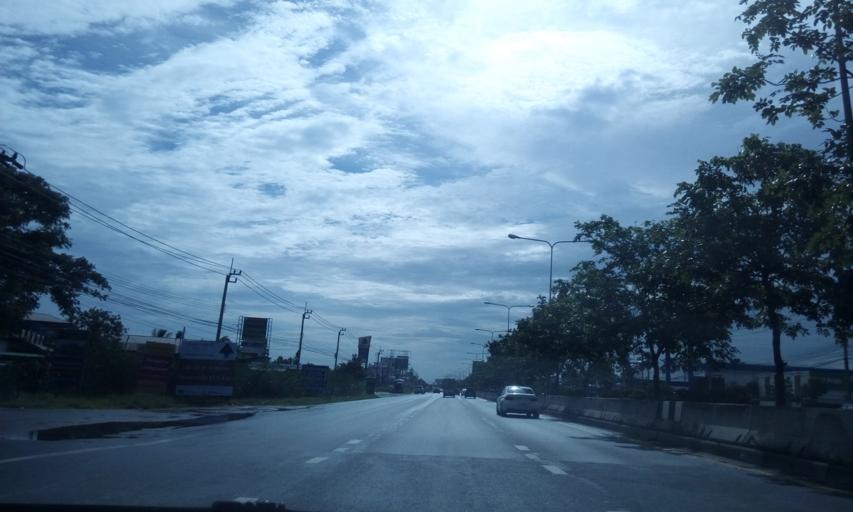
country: TH
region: Nonthaburi
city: Pak Kret
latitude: 13.9226
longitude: 100.4772
